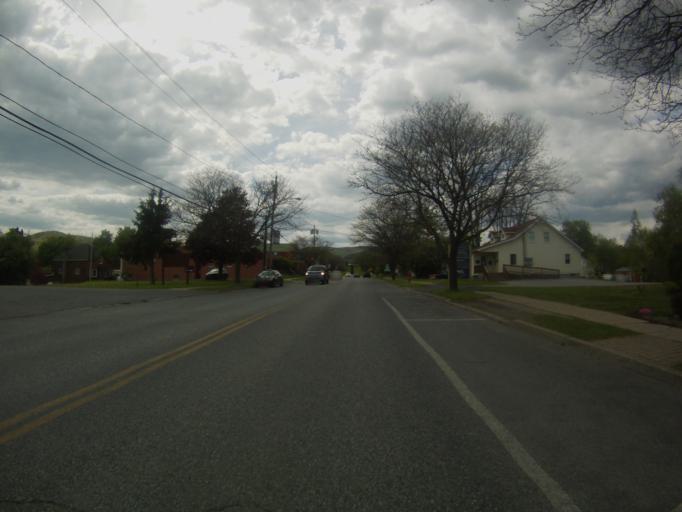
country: US
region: New York
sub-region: Essex County
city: Ticonderoga
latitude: 43.8484
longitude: -73.4323
